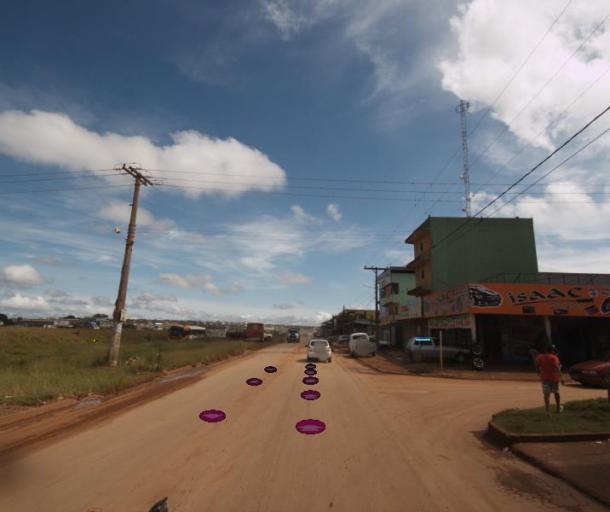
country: BR
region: Federal District
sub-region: Brasilia
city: Brasilia
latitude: -15.7488
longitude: -48.2623
